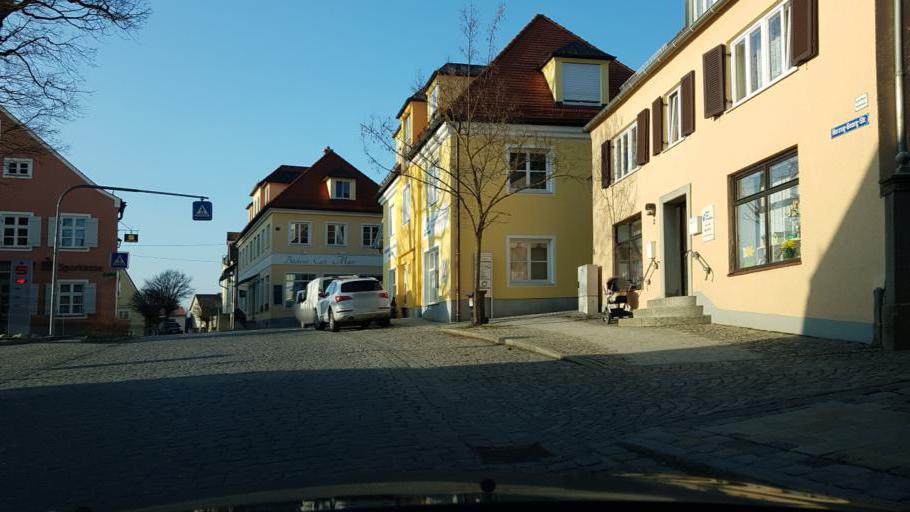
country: DE
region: Bavaria
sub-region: Upper Bavaria
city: Altomunster
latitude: 48.3877
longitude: 11.2561
